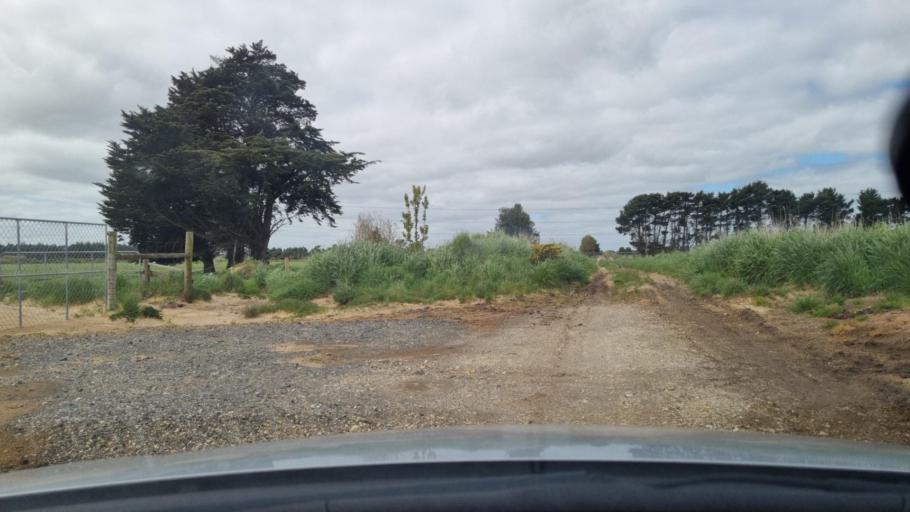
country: NZ
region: Southland
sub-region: Invercargill City
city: Invercargill
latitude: -46.3922
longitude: 168.4597
